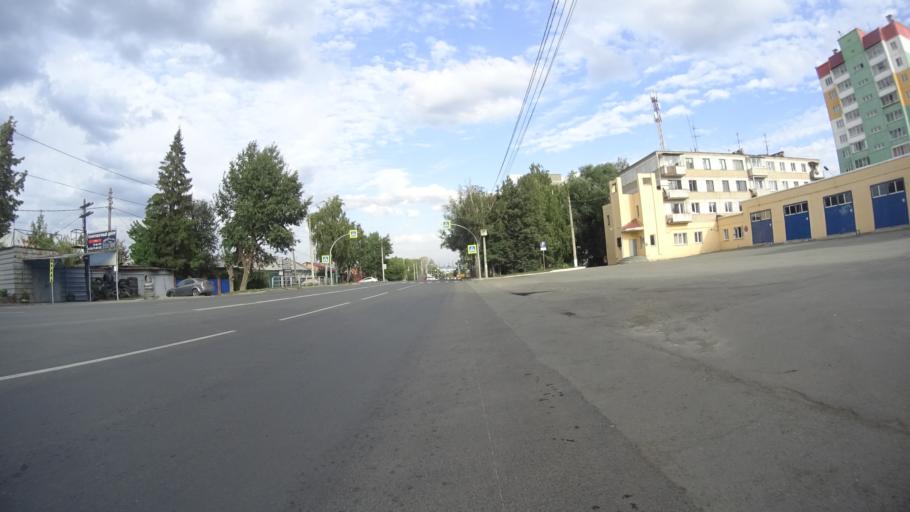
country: RU
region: Chelyabinsk
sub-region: Gorod Chelyabinsk
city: Chelyabinsk
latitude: 55.1984
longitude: 61.3589
